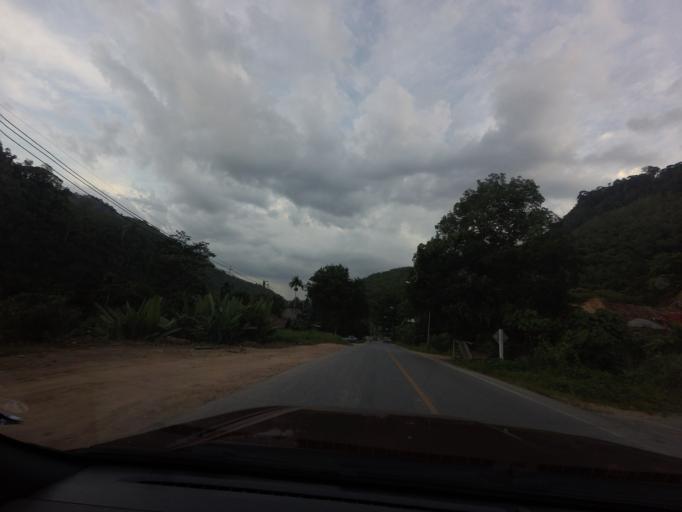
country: TH
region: Yala
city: Than To
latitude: 6.0091
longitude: 101.1949
